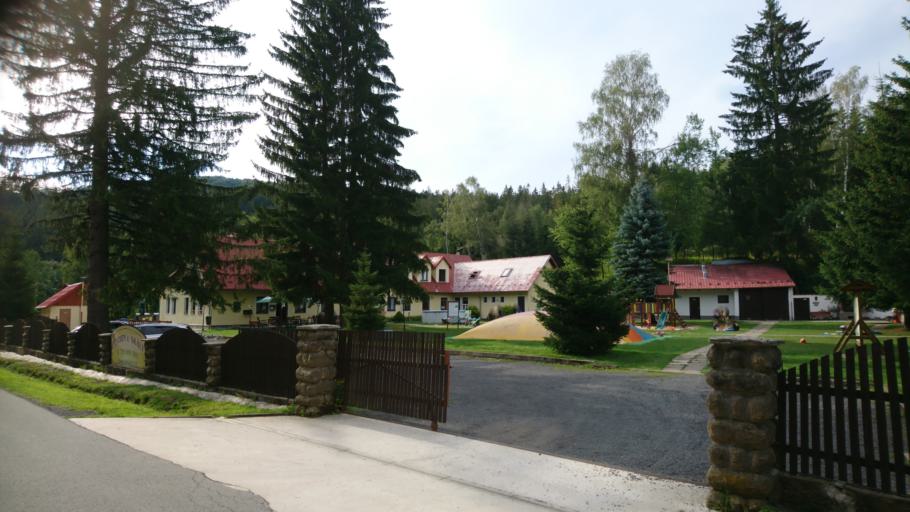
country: CZ
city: Novy Bor
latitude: 50.8216
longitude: 14.5466
